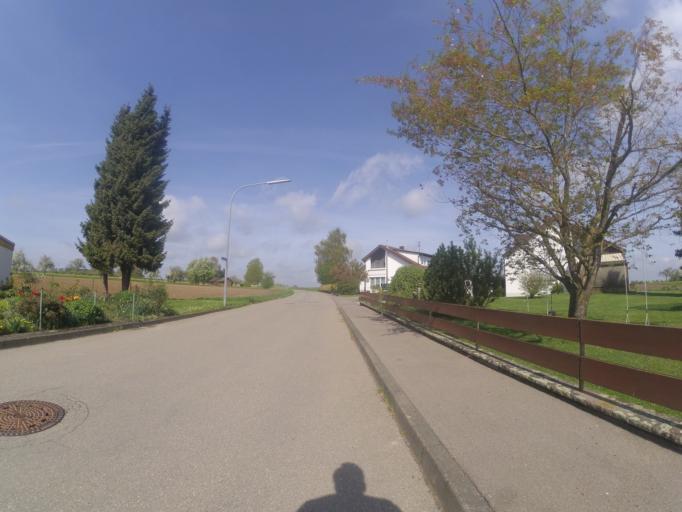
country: DE
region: Baden-Wuerttemberg
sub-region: Tuebingen Region
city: Griesingen
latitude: 48.2304
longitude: 9.8190
